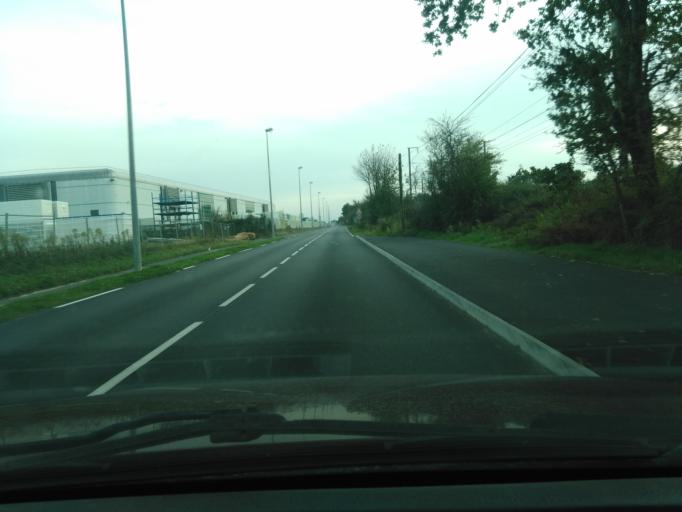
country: FR
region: Pays de la Loire
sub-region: Departement de la Vendee
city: Mouilleron-le-Captif
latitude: 46.7235
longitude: -1.4323
